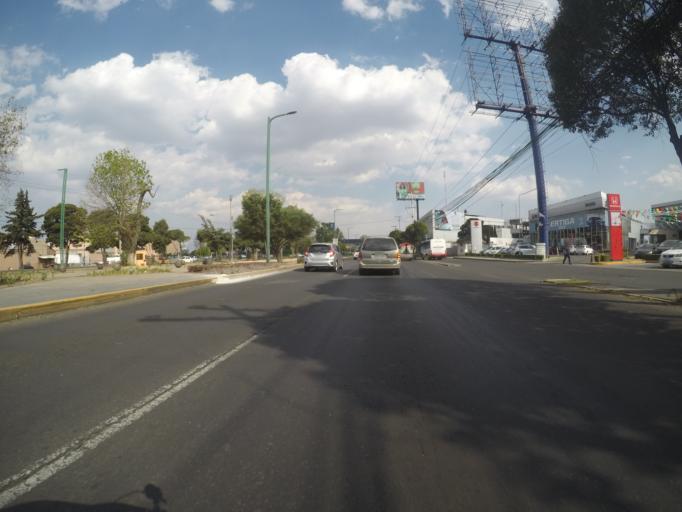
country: MX
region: Mexico
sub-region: Metepec
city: San Jorge Pueblo Nuevo
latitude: 19.2573
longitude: -99.6237
